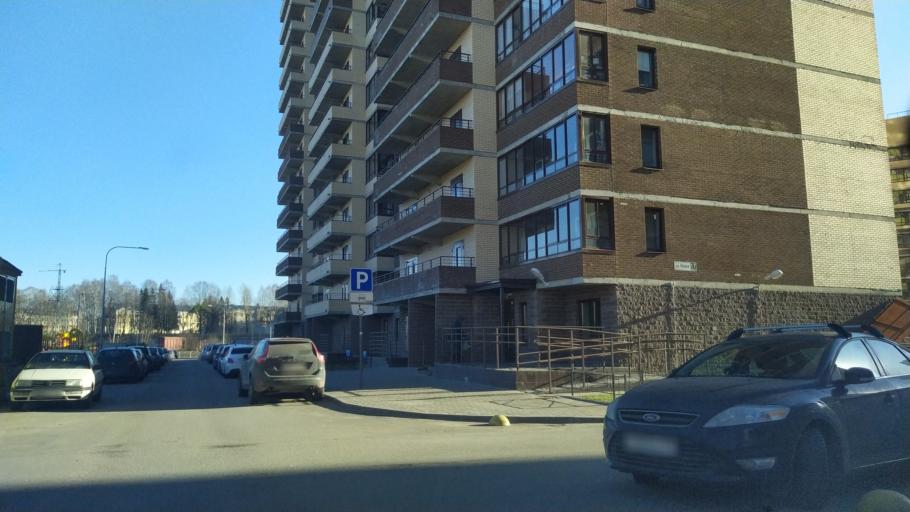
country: RU
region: Leningrad
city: Murino
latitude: 60.0393
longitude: 30.4554
